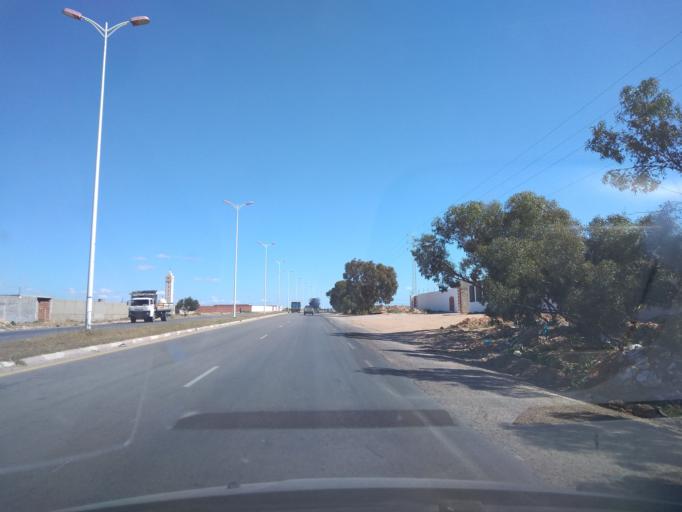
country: TN
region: Safaqis
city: Sfax
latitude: 34.8138
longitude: 10.6974
